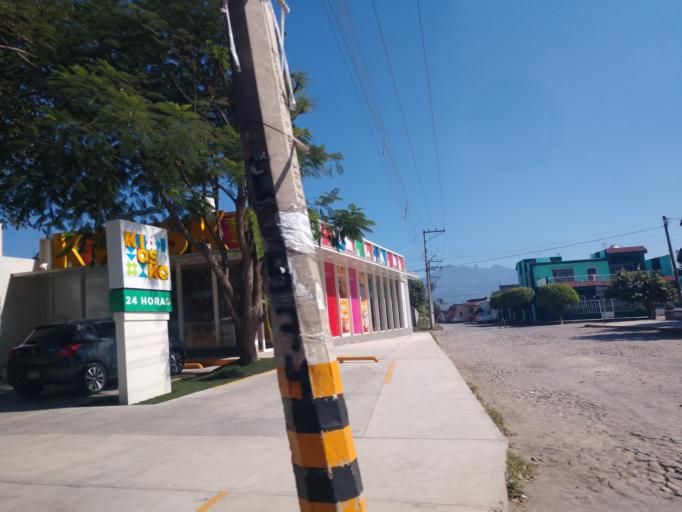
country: MX
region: Nayarit
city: Xalisco
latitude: 21.4736
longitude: -104.8700
